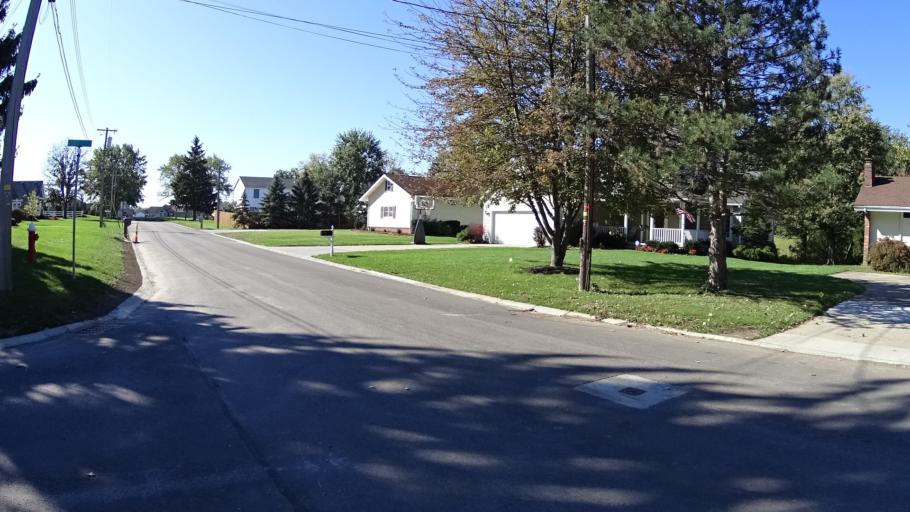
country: US
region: Ohio
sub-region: Lorain County
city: Amherst
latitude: 41.4194
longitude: -82.2213
